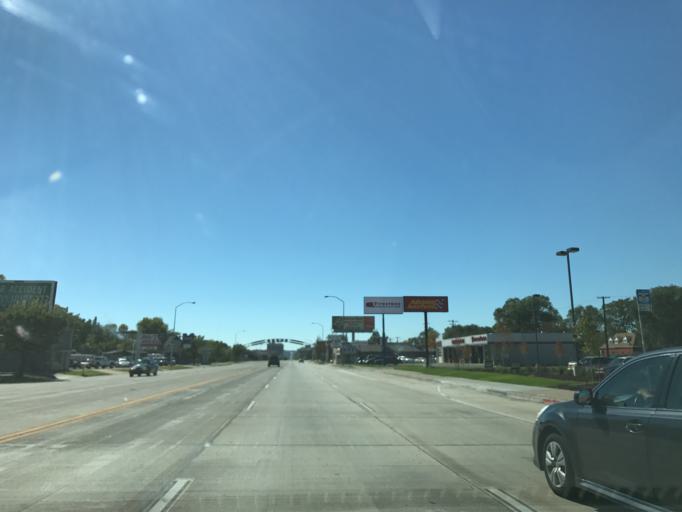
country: US
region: Utah
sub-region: Weber County
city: Ogden
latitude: 41.2365
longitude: -111.9702
